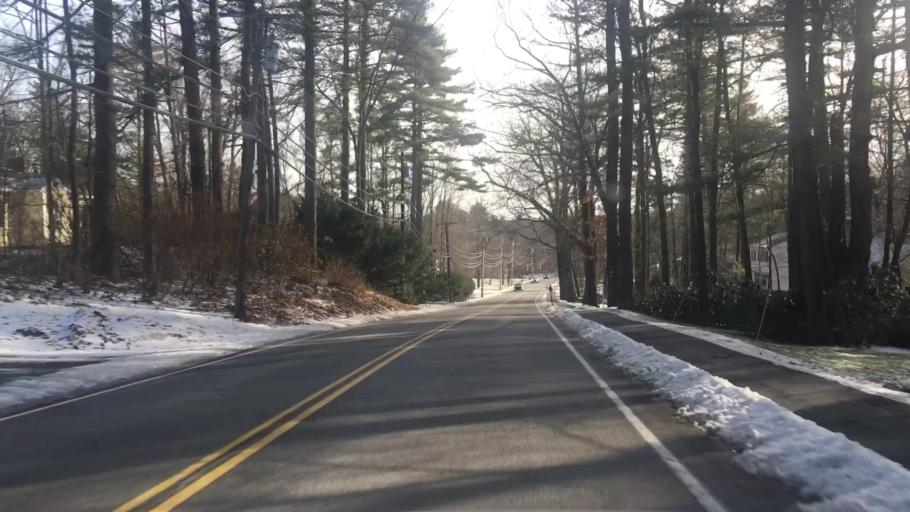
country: US
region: New Hampshire
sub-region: Merrimack County
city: East Concord
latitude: 43.2524
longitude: -71.5410
